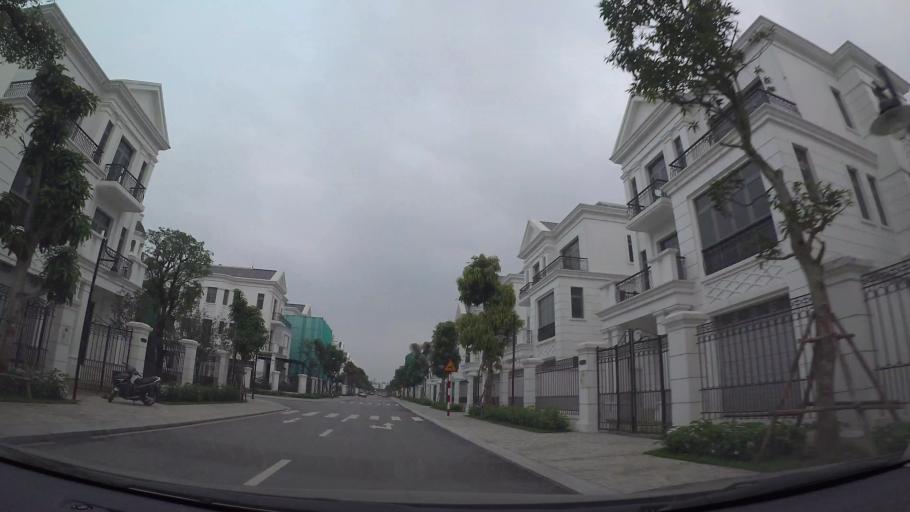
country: VN
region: Ha Noi
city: Trau Quy
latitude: 21.0489
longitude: 105.9022
